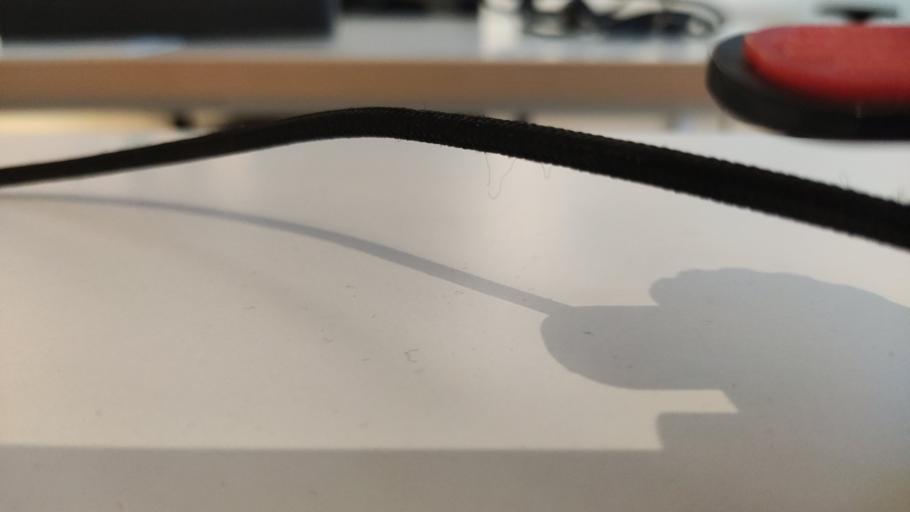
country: RU
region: Moskovskaya
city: Sychevo
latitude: 55.8441
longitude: 36.3383
